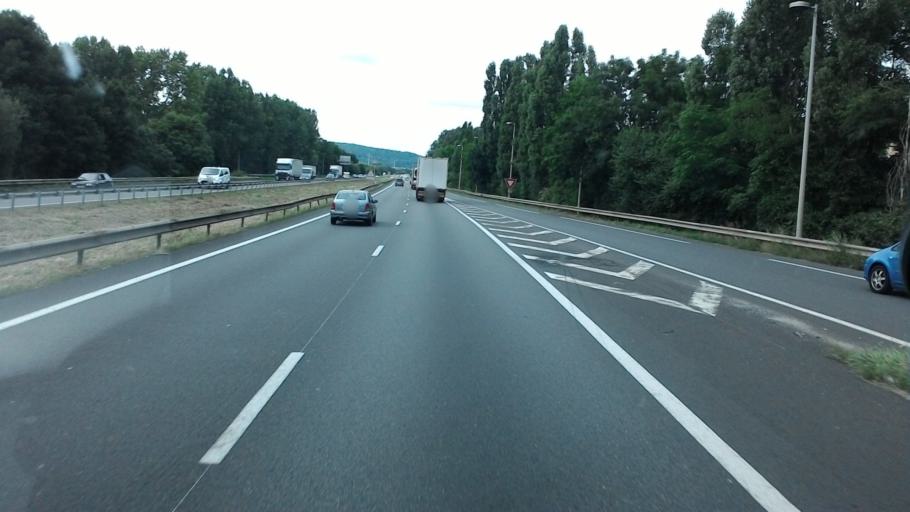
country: FR
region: Lorraine
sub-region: Departement de Meurthe-et-Moselle
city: Bouxieres-aux-Dames
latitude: 48.7547
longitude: 6.1555
